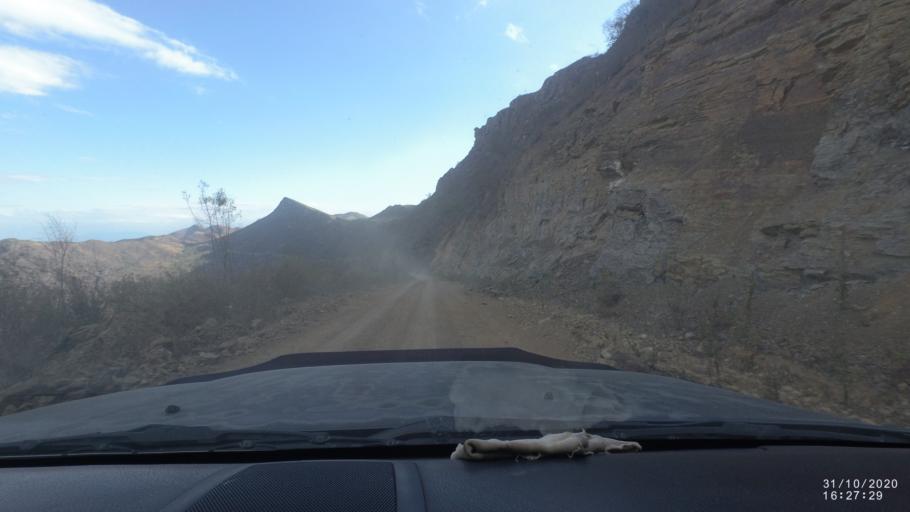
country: BO
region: Chuquisaca
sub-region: Provincia Zudanez
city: Mojocoya
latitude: -18.4065
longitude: -64.5861
